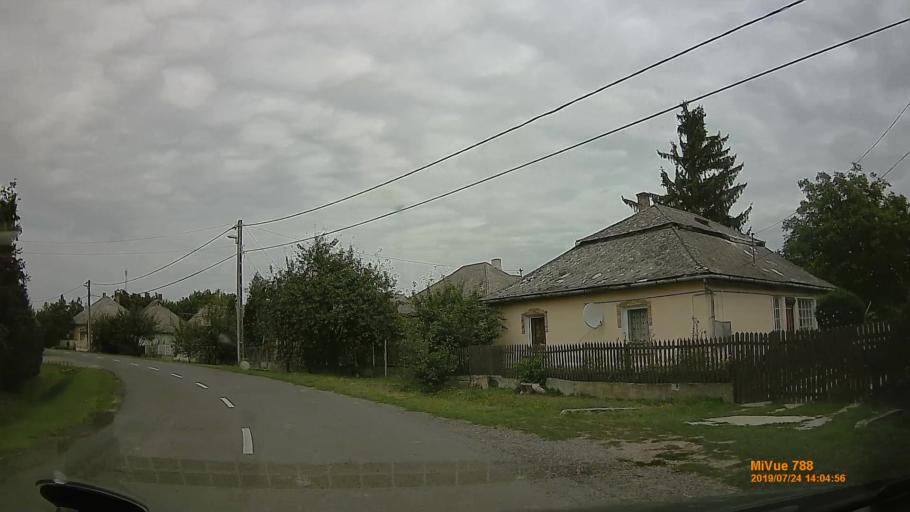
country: HU
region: Szabolcs-Szatmar-Bereg
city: Aranyosapati
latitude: 48.2836
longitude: 22.2826
